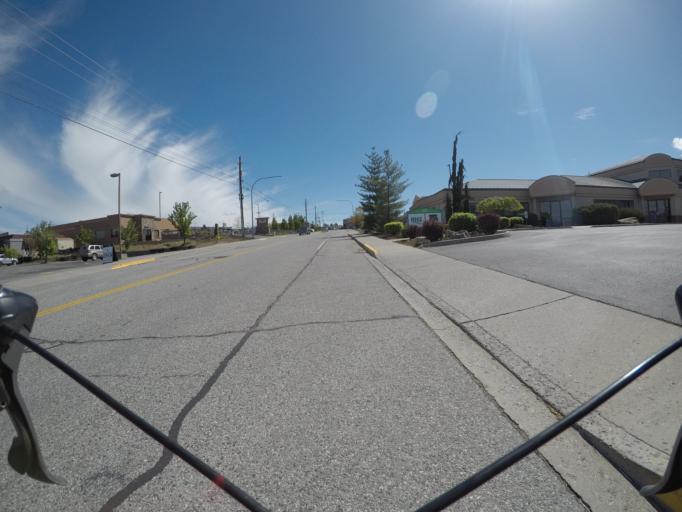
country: US
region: Washington
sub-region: Douglas County
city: East Wenatchee
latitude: 47.4048
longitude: -120.2844
